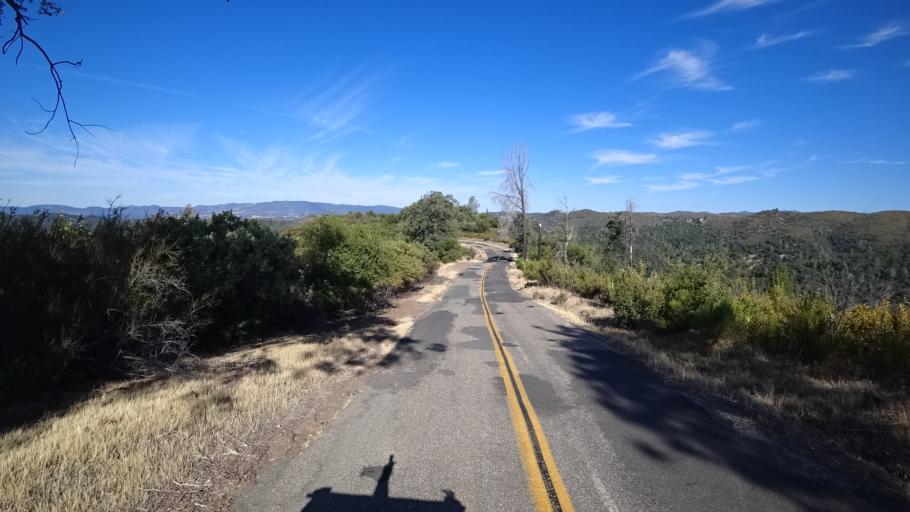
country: US
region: California
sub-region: Calaveras County
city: Mountain Ranch
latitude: 38.1645
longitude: -120.5550
